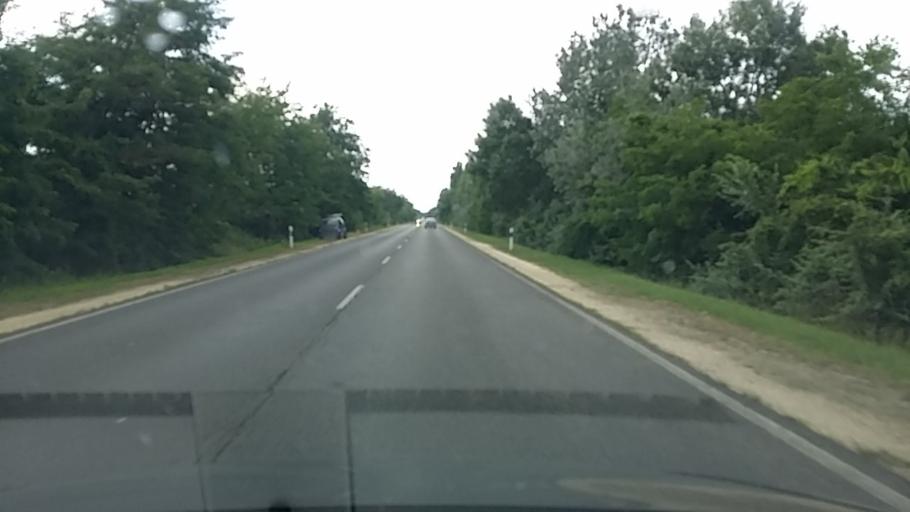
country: HU
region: Pest
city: Orkeny
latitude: 47.1151
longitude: 19.4487
